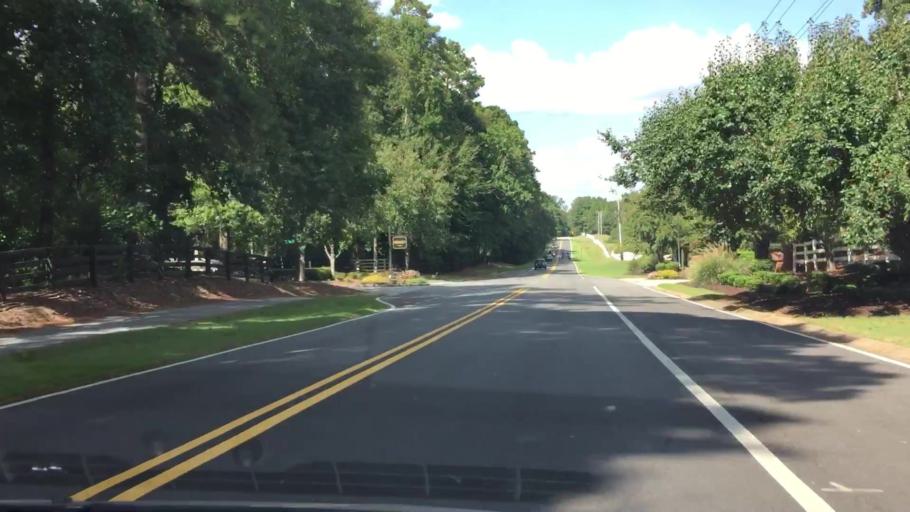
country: US
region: Georgia
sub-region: Fayette County
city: Shannon
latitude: 33.3750
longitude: -84.5164
